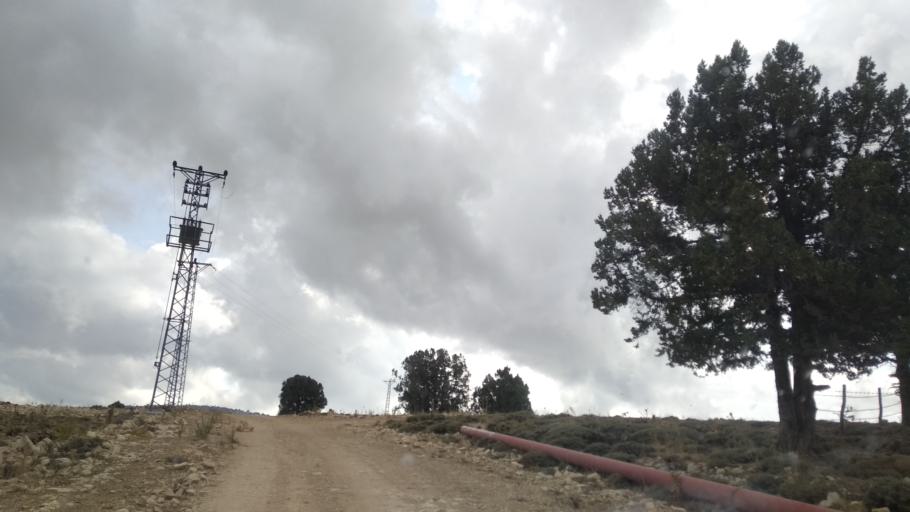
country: TR
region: Mersin
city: Sarikavak
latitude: 36.5722
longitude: 33.7490
